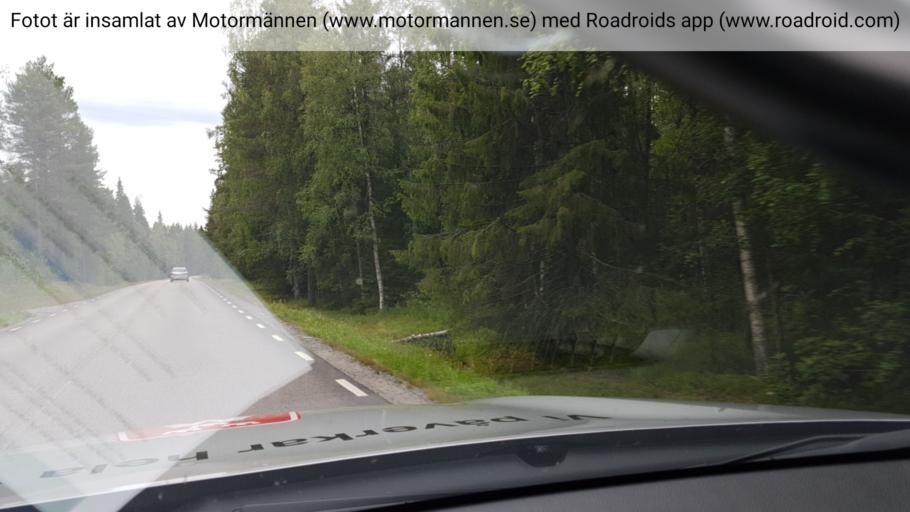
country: SE
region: Norrbotten
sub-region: Lulea Kommun
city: Gammelstad
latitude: 65.6597
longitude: 22.0545
